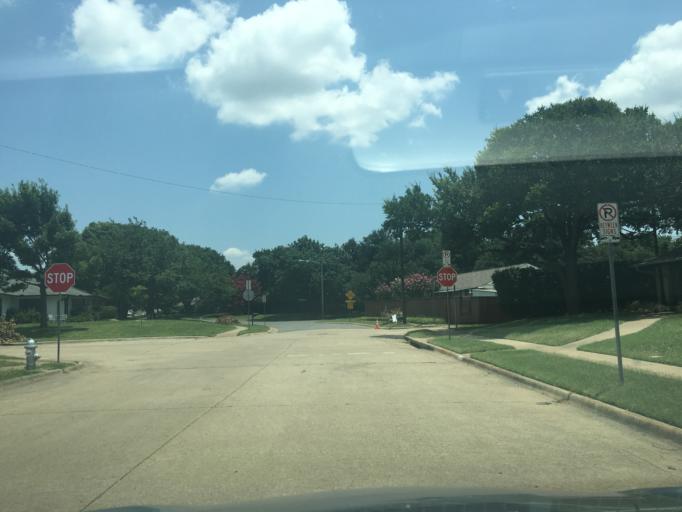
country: US
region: Texas
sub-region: Dallas County
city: Addison
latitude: 32.9161
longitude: -96.8442
